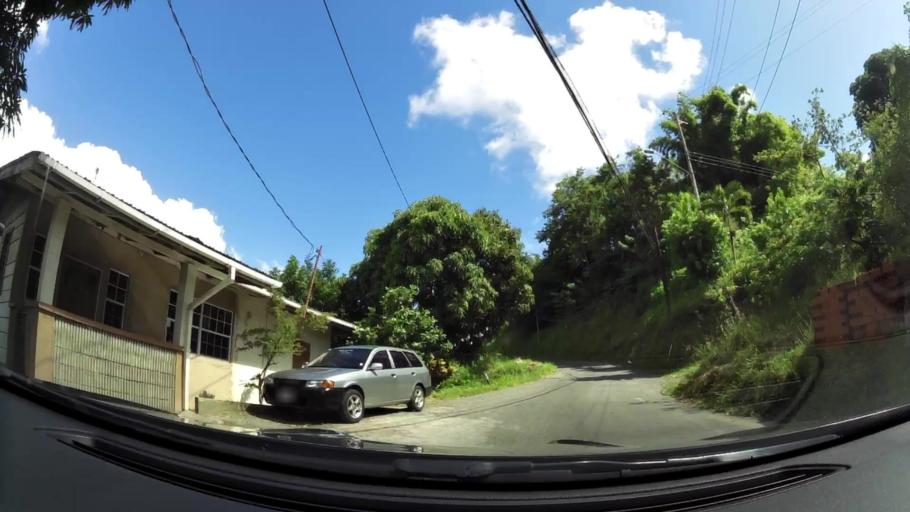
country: TT
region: Tobago
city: Scarborough
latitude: 11.2448
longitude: -60.7300
